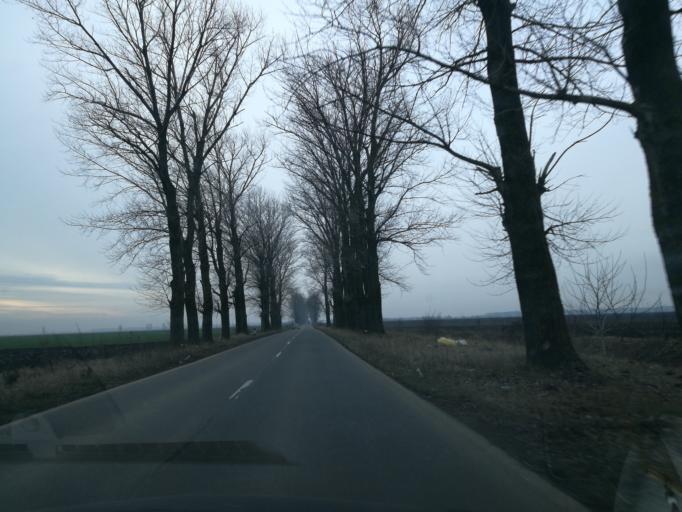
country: RO
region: Ilfov
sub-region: Comuna Gradistea
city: Gradistea
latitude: 44.6227
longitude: 26.2838
